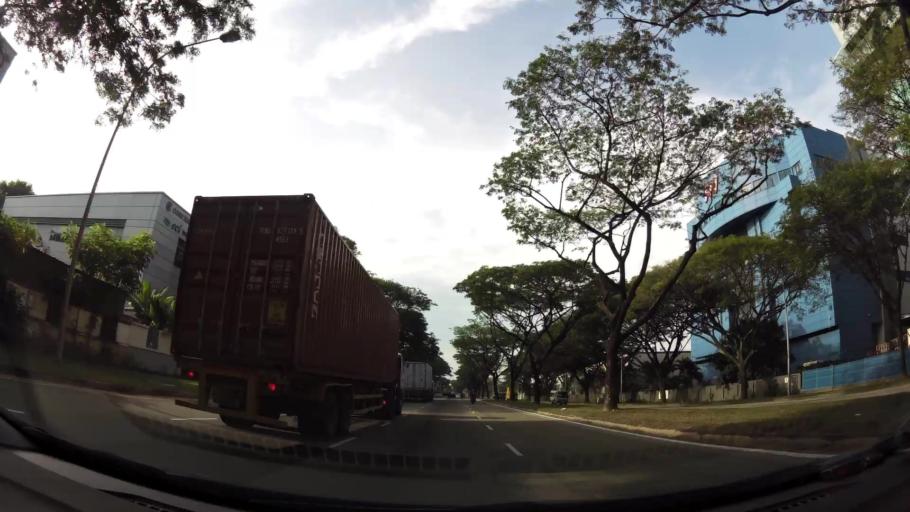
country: MY
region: Johor
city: Johor Bahru
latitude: 1.3113
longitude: 103.6277
